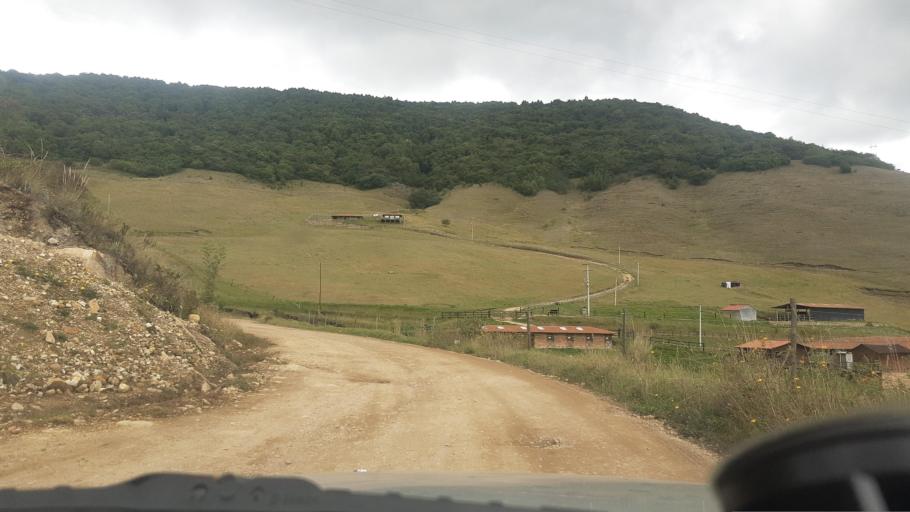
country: CO
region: Cundinamarca
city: Suesca
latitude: 5.1593
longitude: -73.8013
